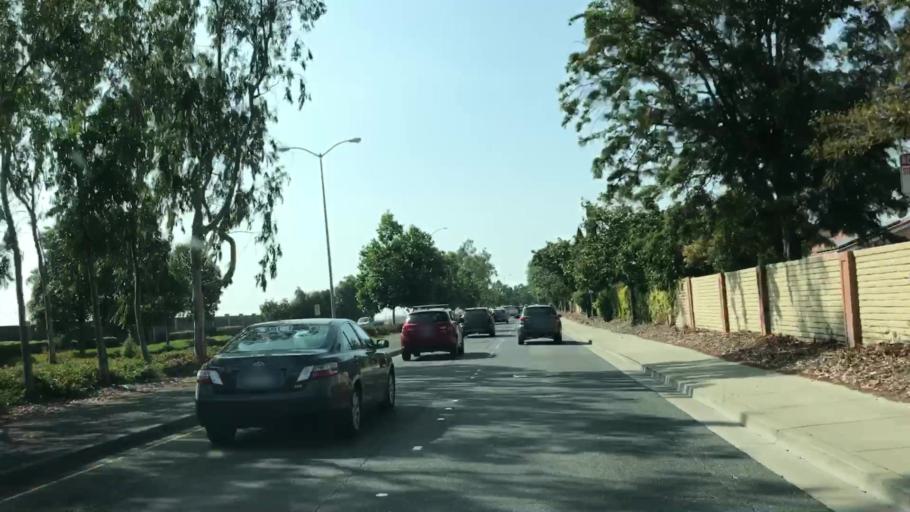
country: US
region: California
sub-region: Alameda County
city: Newark
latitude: 37.5688
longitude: -122.0736
